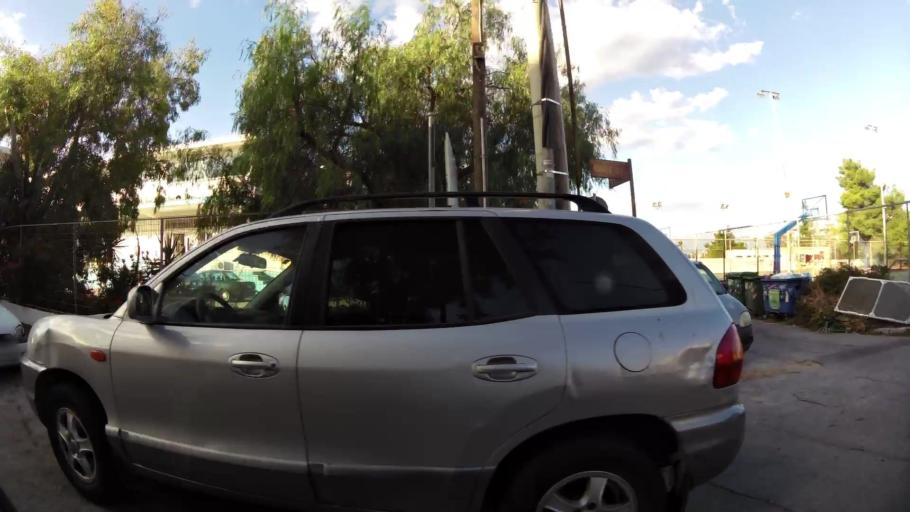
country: GR
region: Attica
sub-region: Nomarchia Athinas
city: Elliniko
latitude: 37.8899
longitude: 23.7450
